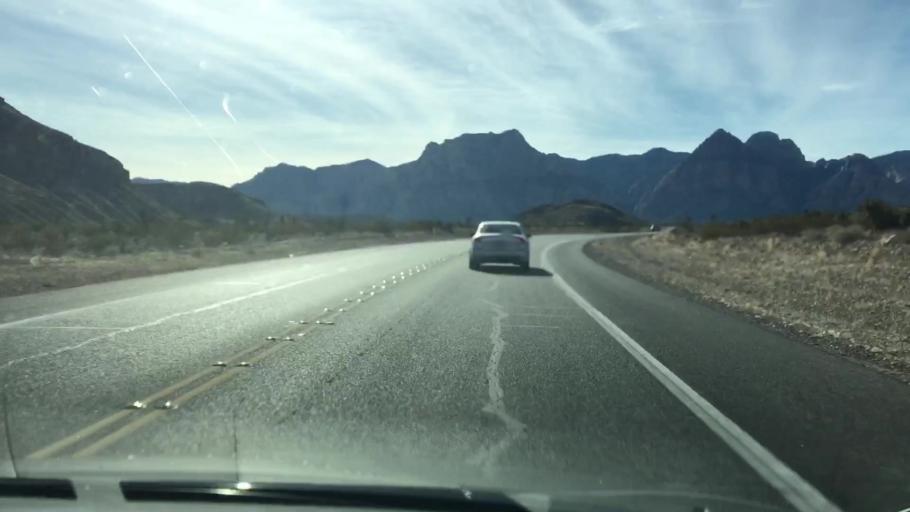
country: US
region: Nevada
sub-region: Clark County
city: Summerlin South
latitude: 36.1341
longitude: -115.4118
